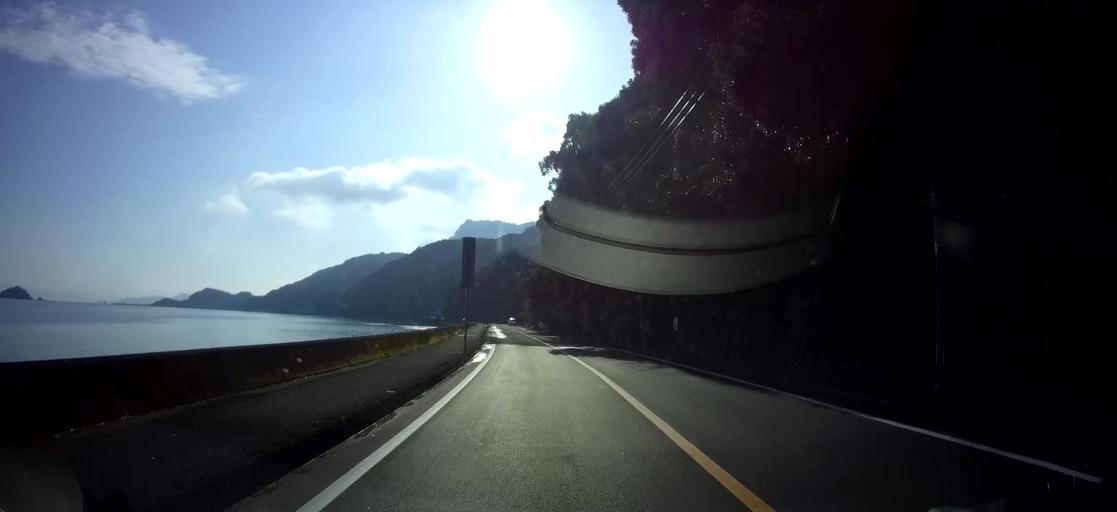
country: JP
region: Kumamoto
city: Yatsushiro
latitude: 32.4898
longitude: 130.4401
